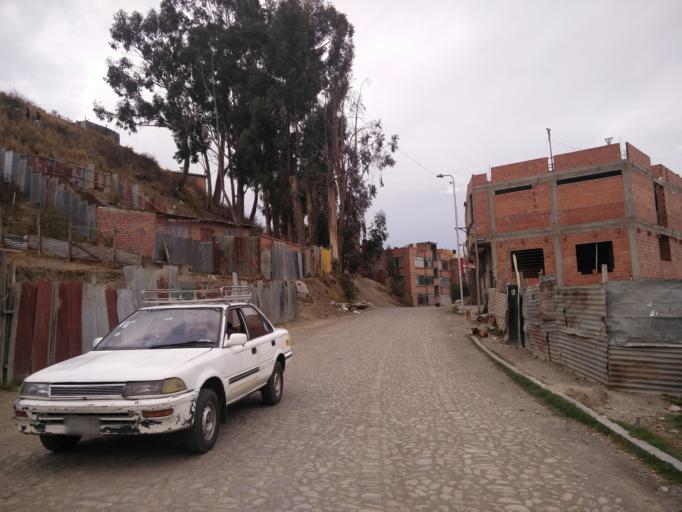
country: BO
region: La Paz
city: La Paz
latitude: -16.5198
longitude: -68.1291
